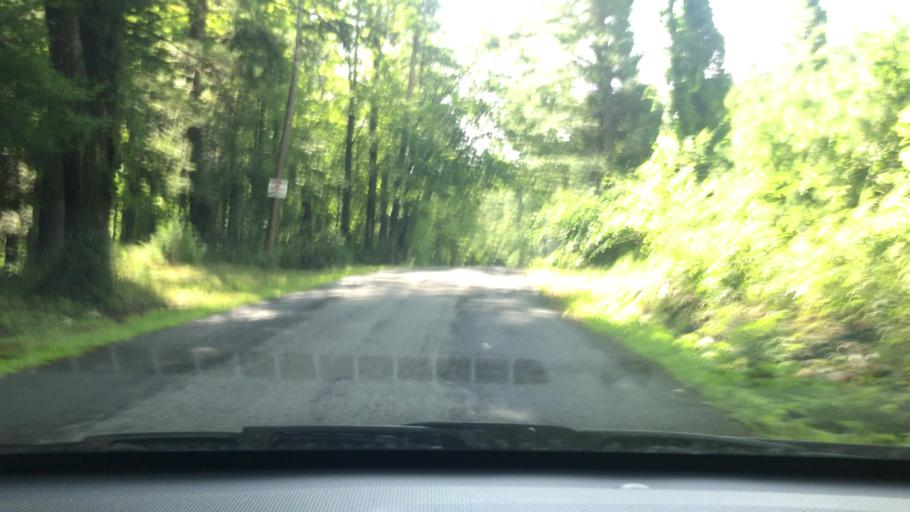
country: US
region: New York
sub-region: Ulster County
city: Shokan
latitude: 41.9657
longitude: -74.2857
